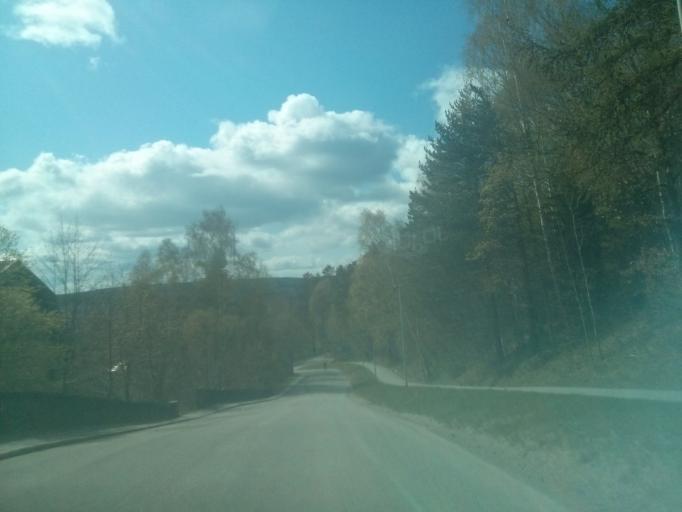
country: SE
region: Vaesternorrland
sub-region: Sundsvalls Kommun
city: Sundsvall
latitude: 62.3970
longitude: 17.3083
